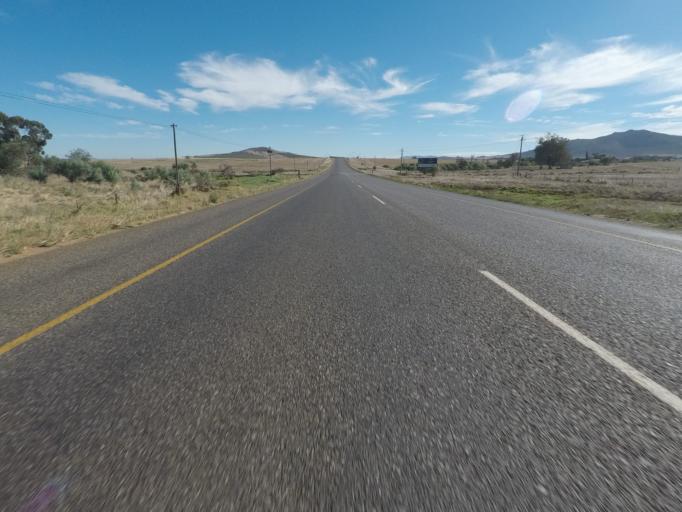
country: ZA
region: Western Cape
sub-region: West Coast District Municipality
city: Malmesbury
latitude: -33.6152
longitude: 18.7270
